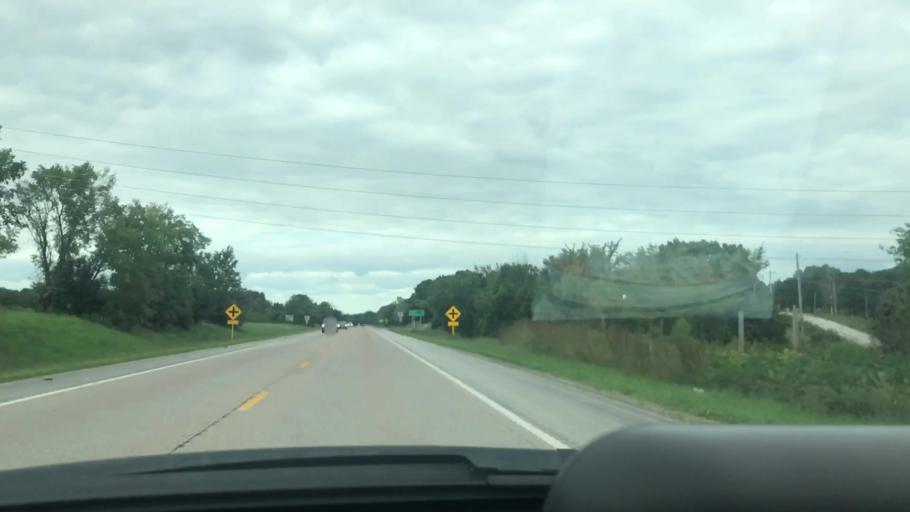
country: US
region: Missouri
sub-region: Benton County
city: Warsaw
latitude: 38.1938
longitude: -93.3246
